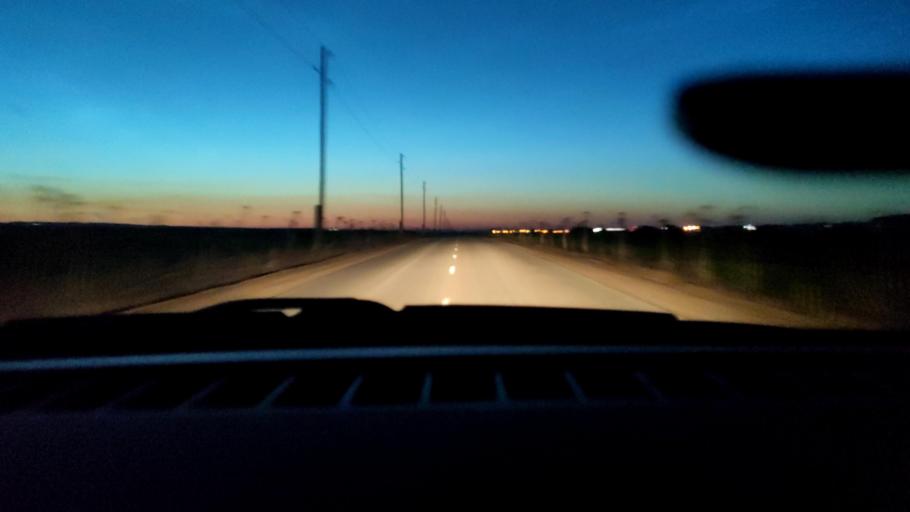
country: RU
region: Perm
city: Kultayevo
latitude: 57.8851
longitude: 55.9893
